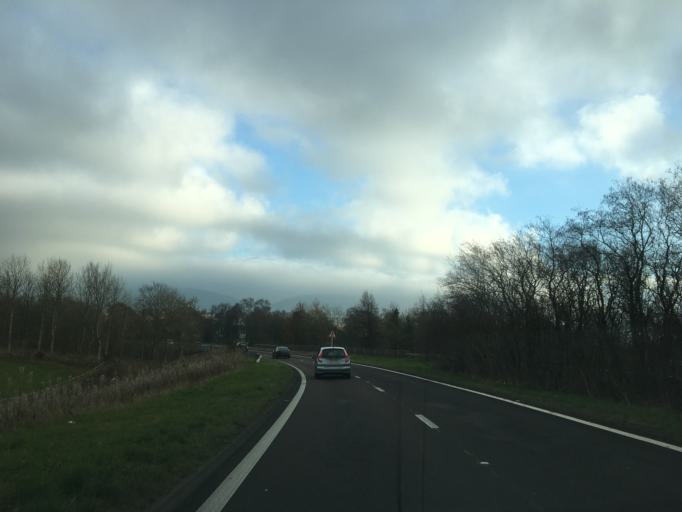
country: GB
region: Scotland
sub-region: Perth and Kinross
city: Milnathort
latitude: 56.2420
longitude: -3.3844
